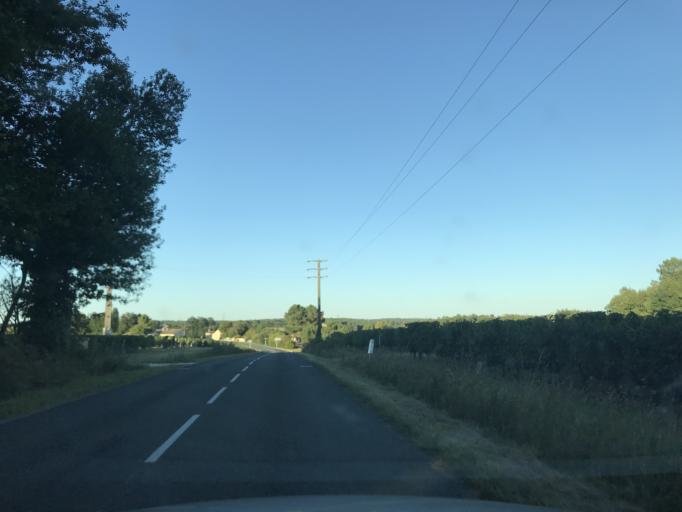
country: FR
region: Aquitaine
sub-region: Departement de la Gironde
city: Lussac
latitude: 44.9748
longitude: -0.0670
